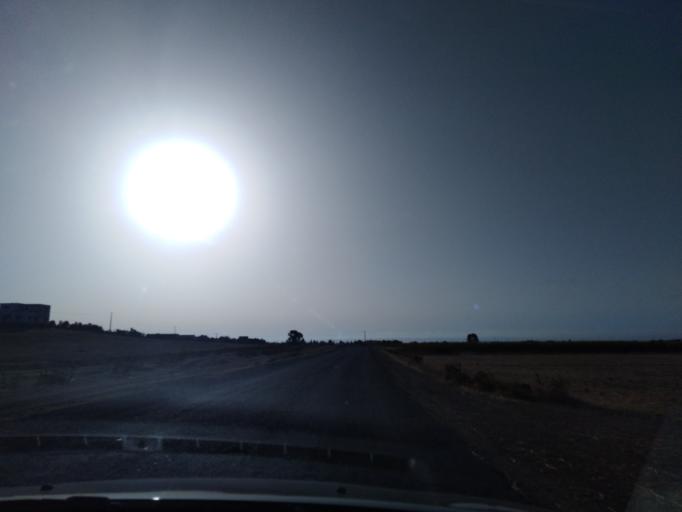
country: MA
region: Doukkala-Abda
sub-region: Safi
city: Safi
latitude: 32.4737
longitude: -8.8684
